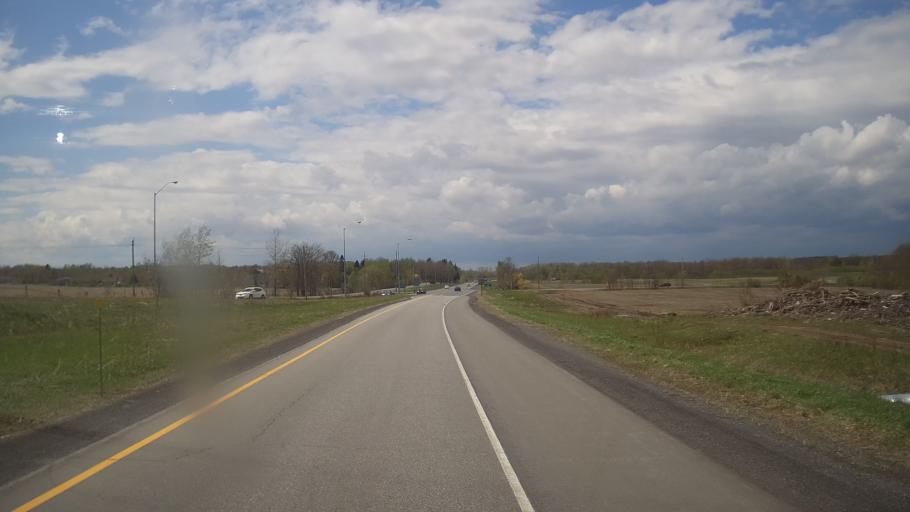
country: CA
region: Ontario
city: Hawkesbury
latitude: 45.5668
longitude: -74.5057
